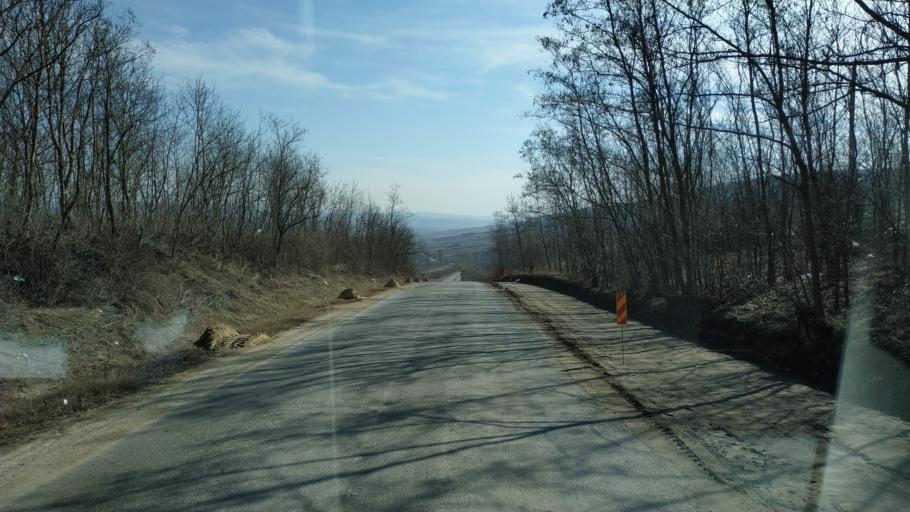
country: MD
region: Nisporeni
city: Nisporeni
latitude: 47.1912
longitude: 28.0674
